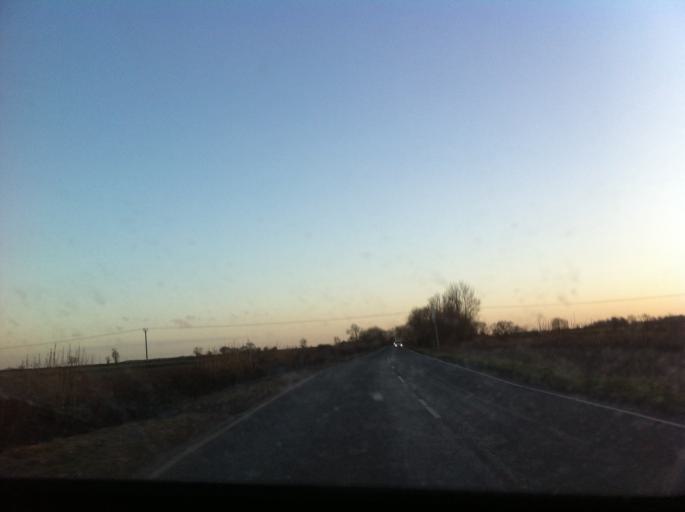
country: GB
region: England
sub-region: Northamptonshire
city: Irchester
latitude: 52.2738
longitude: -0.6547
